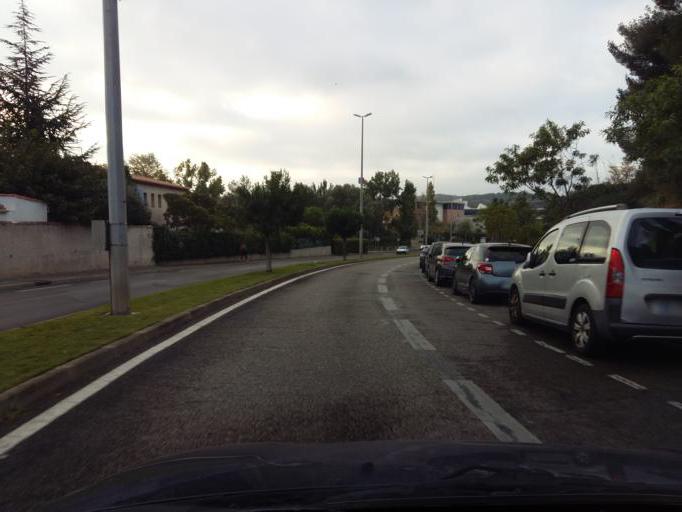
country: FR
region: Provence-Alpes-Cote d'Azur
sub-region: Departement des Bouches-du-Rhone
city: Martigues
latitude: 43.4083
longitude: 5.0467
